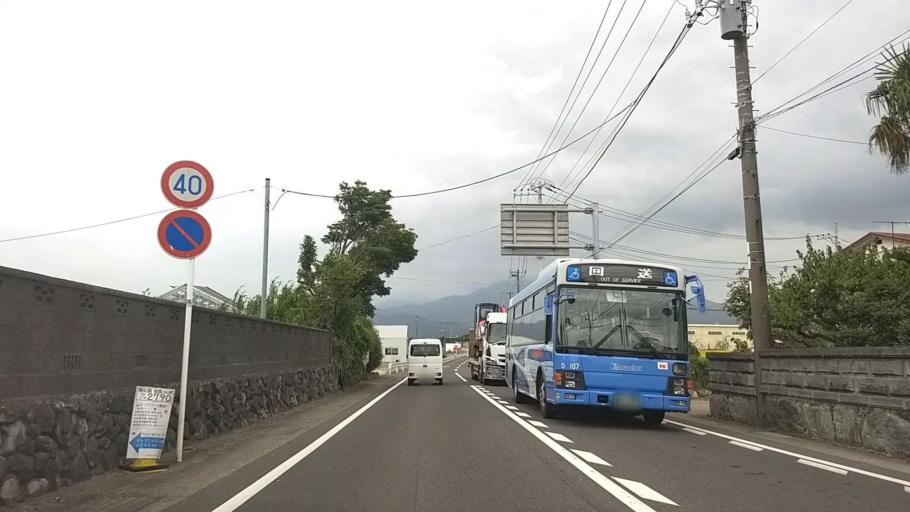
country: JP
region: Kanagawa
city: Isehara
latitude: 35.3831
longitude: 139.3386
